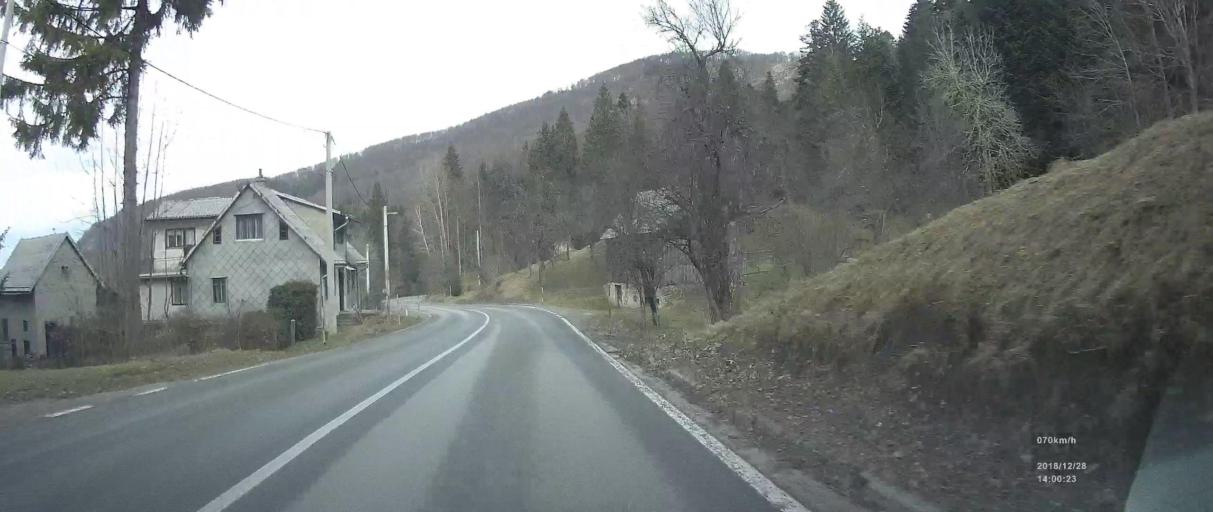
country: SI
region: Kostel
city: Kostel
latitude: 45.4113
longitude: 14.9135
